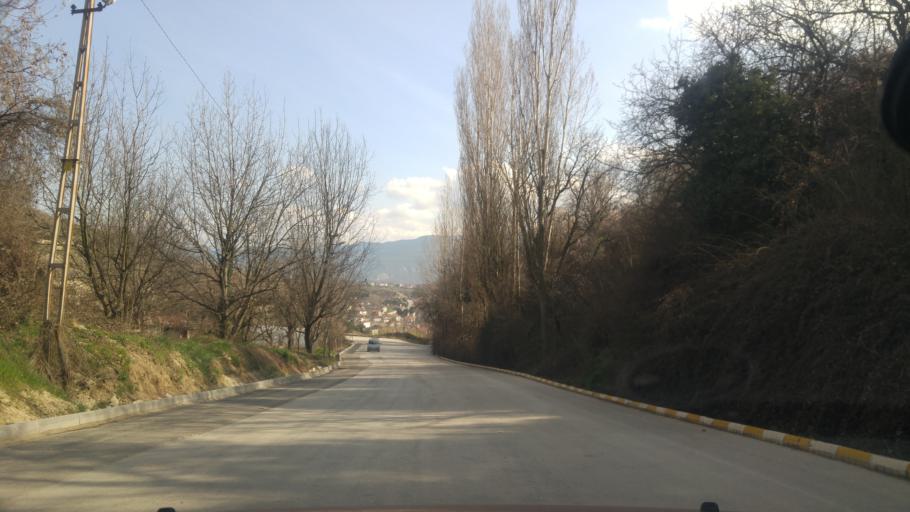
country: TR
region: Karabuk
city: Safranbolu
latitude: 41.2576
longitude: 32.6817
